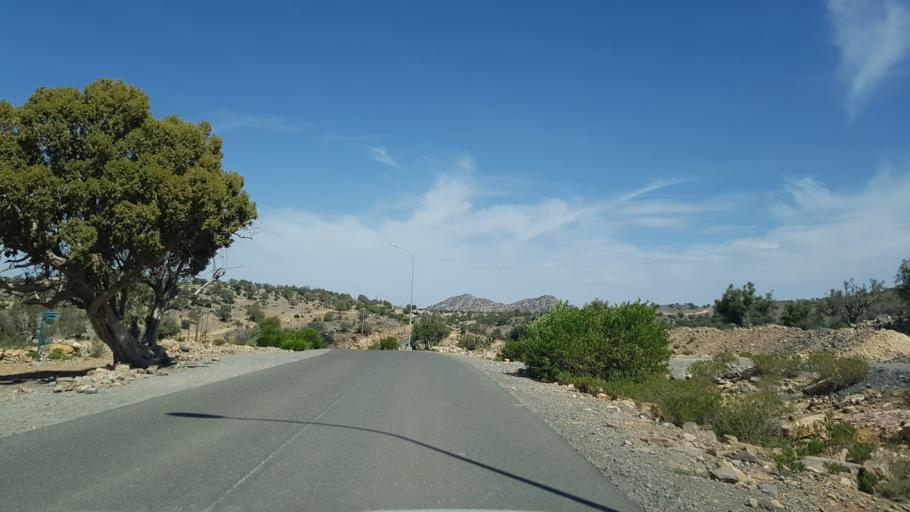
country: OM
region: Al Batinah
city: Bayt al `Awabi
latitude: 23.1216
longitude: 57.6137
